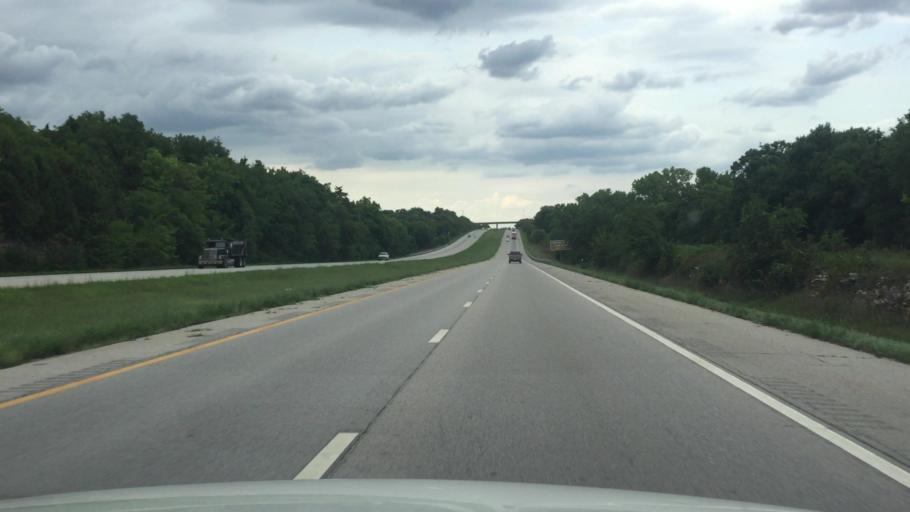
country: US
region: Missouri
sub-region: Cass County
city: Belton
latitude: 38.7889
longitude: -94.6768
